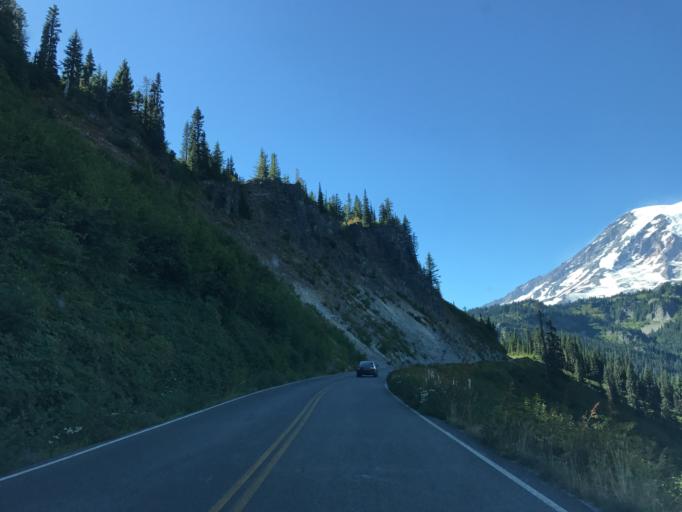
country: US
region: Washington
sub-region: Pierce County
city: Buckley
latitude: 46.7641
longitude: -121.6974
